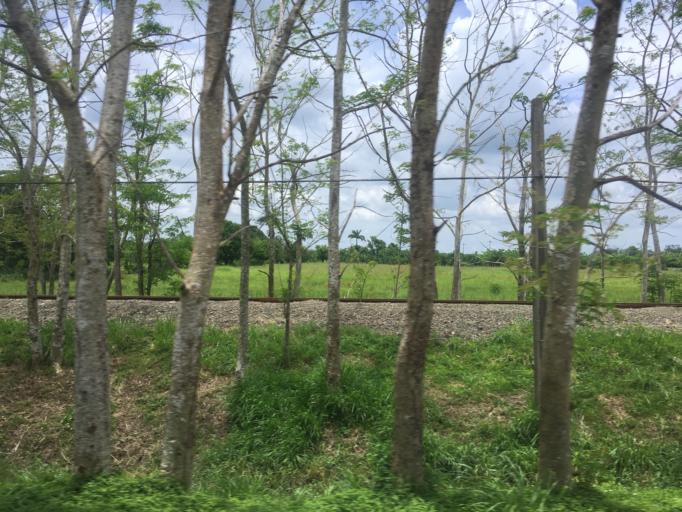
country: CU
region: Villa Clara
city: Esperanza
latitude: 22.4334
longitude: -80.0658
